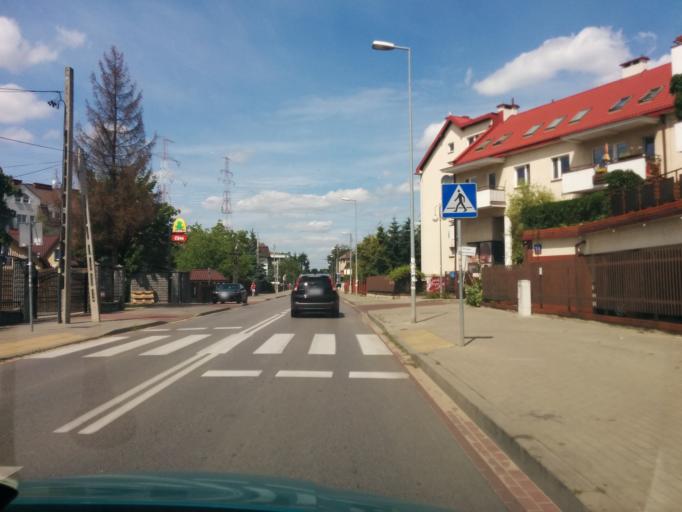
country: PL
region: Masovian Voivodeship
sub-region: Warszawa
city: Bielany
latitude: 52.3212
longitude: 20.9401
